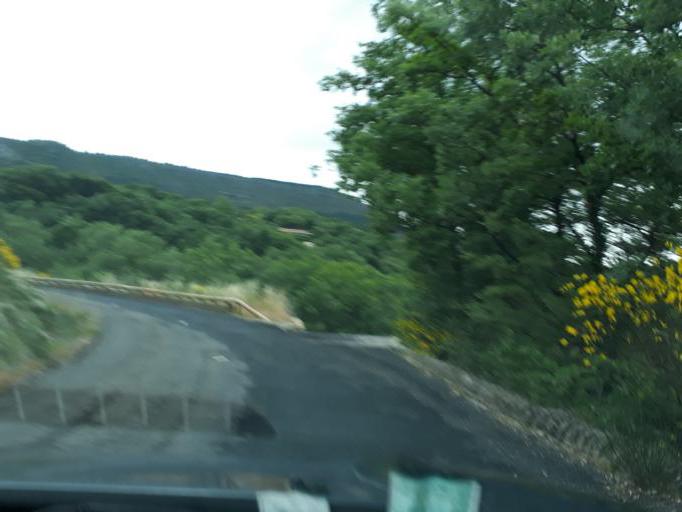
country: FR
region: Languedoc-Roussillon
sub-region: Departement de l'Herault
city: Lodeve
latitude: 43.7640
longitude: 3.3130
